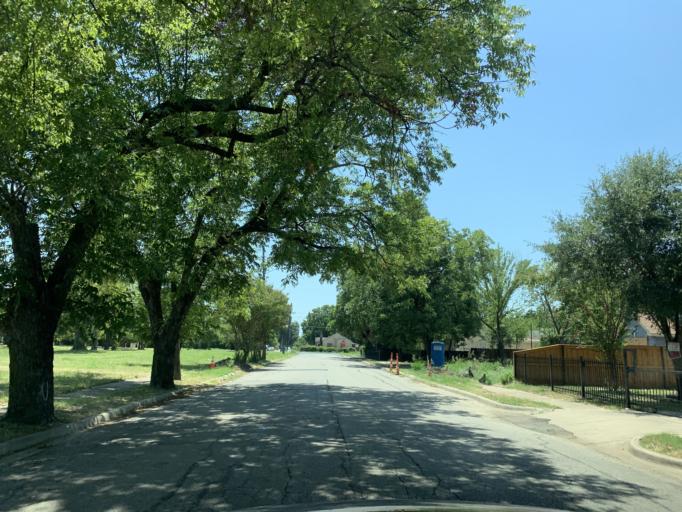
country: US
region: Texas
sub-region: Dallas County
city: Dallas
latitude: 32.6926
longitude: -96.7940
